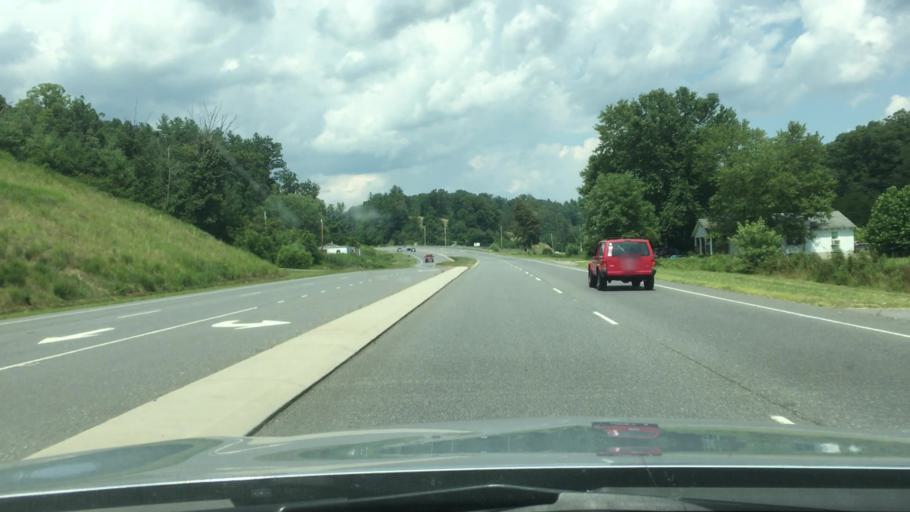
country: US
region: North Carolina
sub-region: Madison County
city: Mars Hill
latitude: 35.8425
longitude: -82.5035
